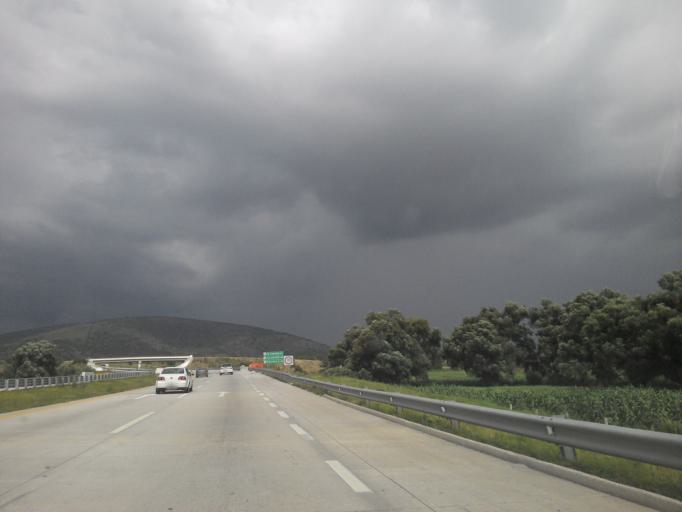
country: MX
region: Mexico
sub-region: Hueypoxtla
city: Santa Maria Ajoloapan
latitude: 19.9551
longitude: -99.0501
